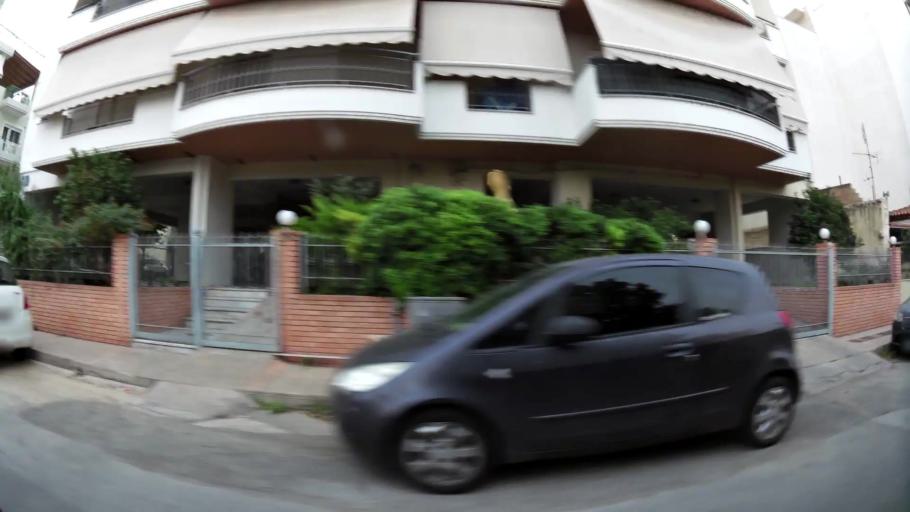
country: GR
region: Attica
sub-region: Nomarchia Athinas
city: Athens
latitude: 37.9783
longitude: 23.7038
